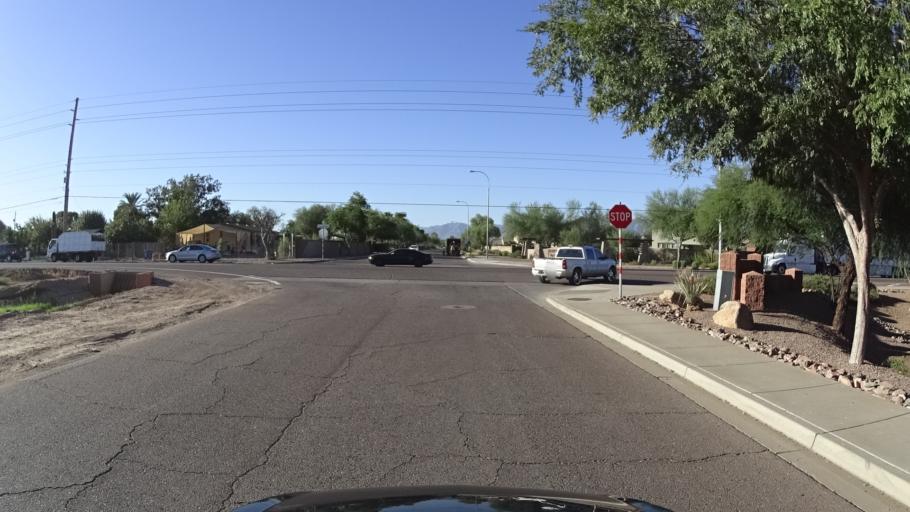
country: US
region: Arizona
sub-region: Maricopa County
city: Tolleson
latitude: 33.4232
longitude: -112.2127
